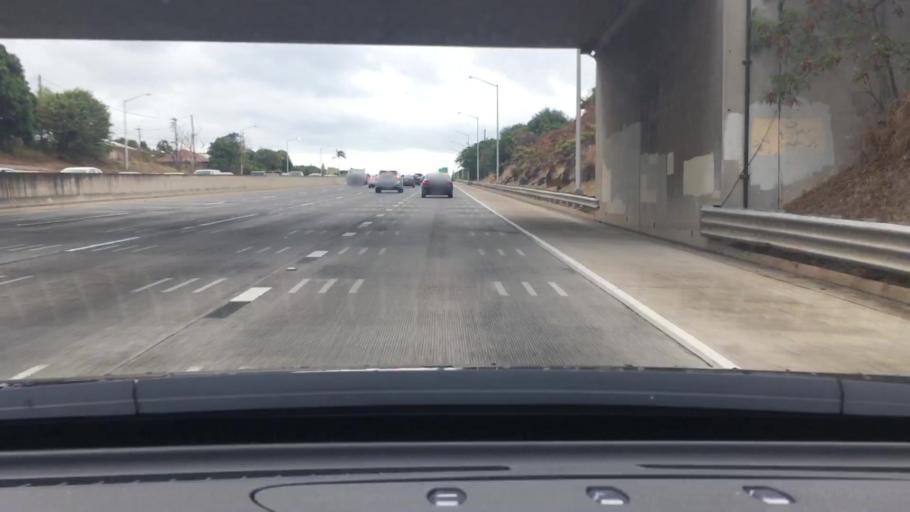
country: US
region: Hawaii
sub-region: Honolulu County
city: Honolulu
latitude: 21.2832
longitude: -157.8062
